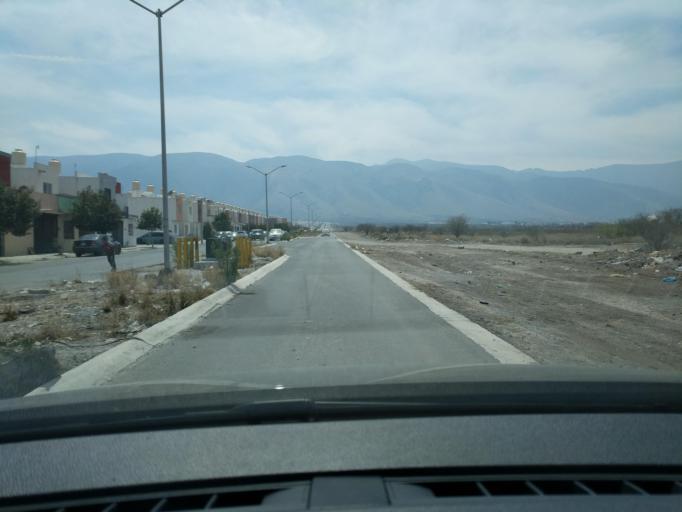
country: MX
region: Coahuila
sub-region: Arteaga
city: Arteaga
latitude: 25.4259
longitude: -100.9128
